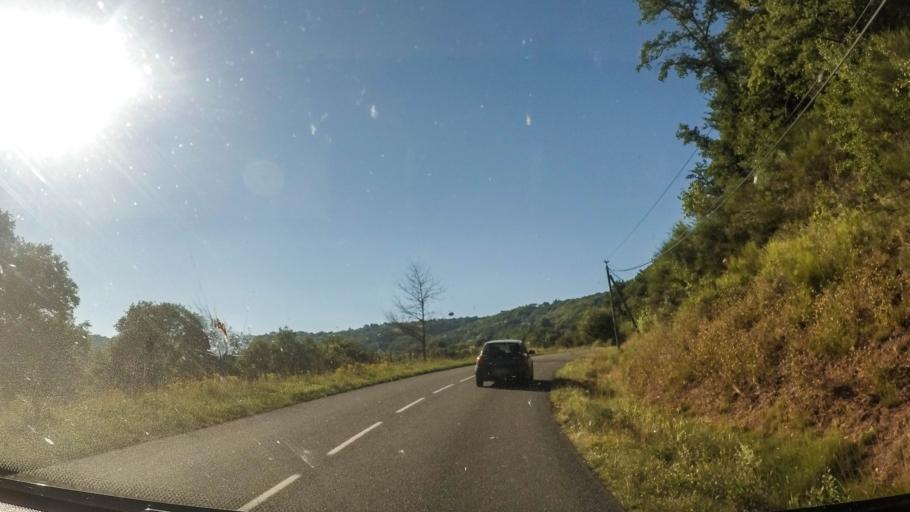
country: FR
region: Midi-Pyrenees
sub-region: Departement de l'Aveyron
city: Saint-Christophe-Vallon
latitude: 44.5540
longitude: 2.3950
